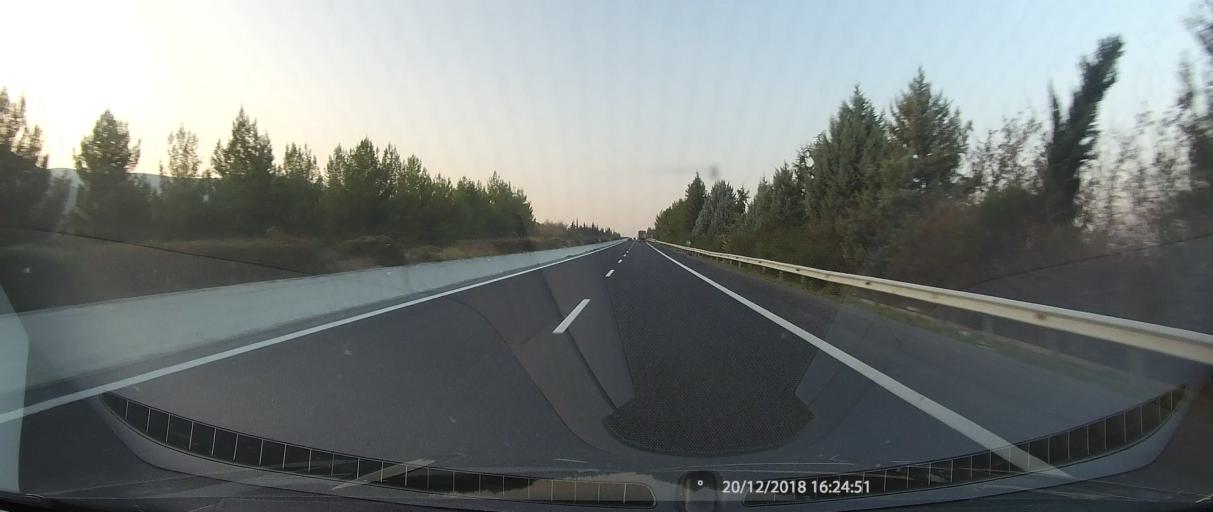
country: GR
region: Thessaly
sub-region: Nomos Magnisias
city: Sourpi
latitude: 39.1169
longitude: 22.8528
